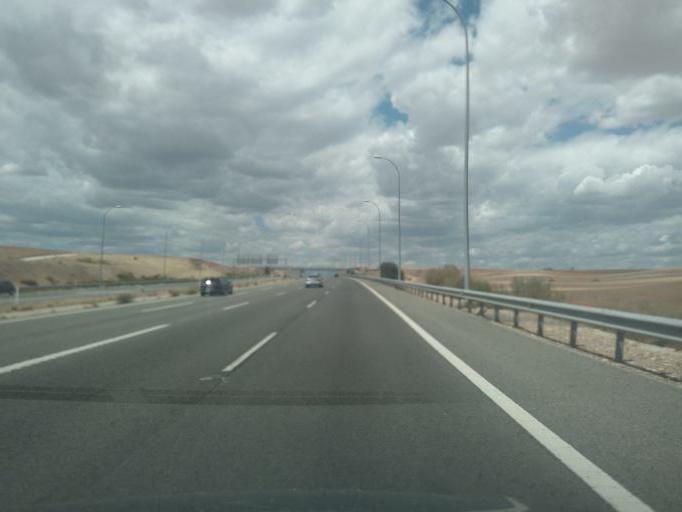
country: ES
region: Madrid
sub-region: Provincia de Madrid
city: Paracuellos de Jarama
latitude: 40.5223
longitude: -3.5073
